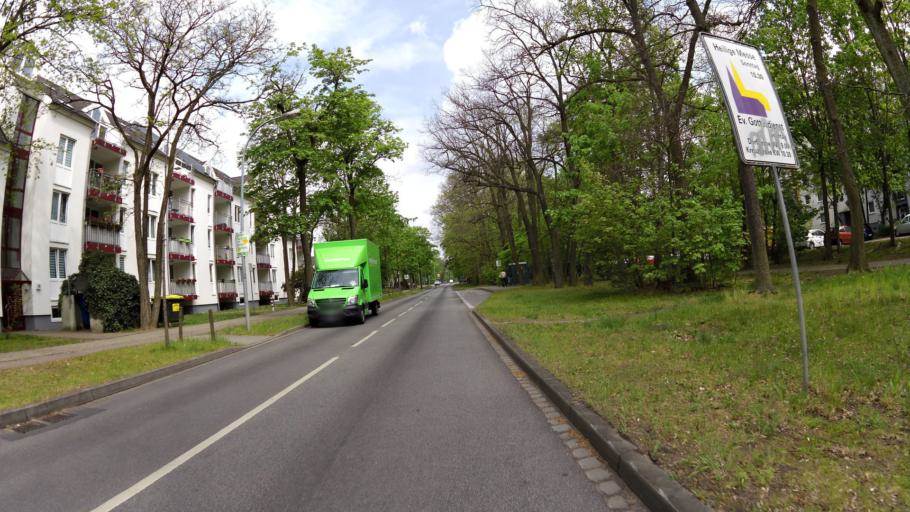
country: DE
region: Brandenburg
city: Konigs Wusterhausen
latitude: 52.2849
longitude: 13.6147
